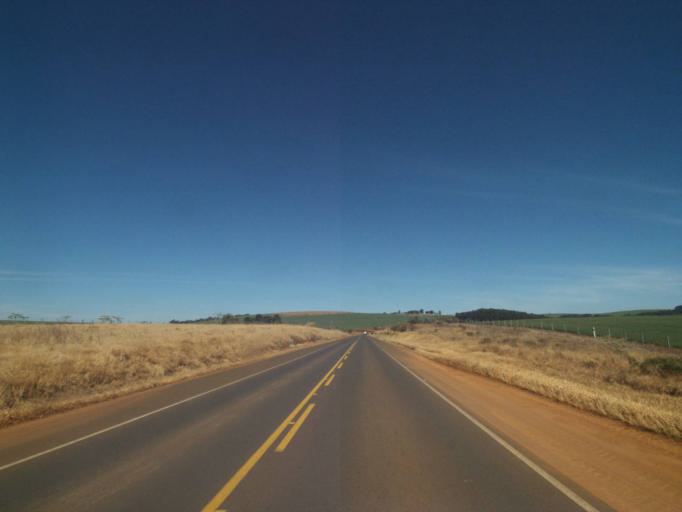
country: BR
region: Parana
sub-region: Tibagi
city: Tibagi
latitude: -24.7413
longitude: -50.4597
